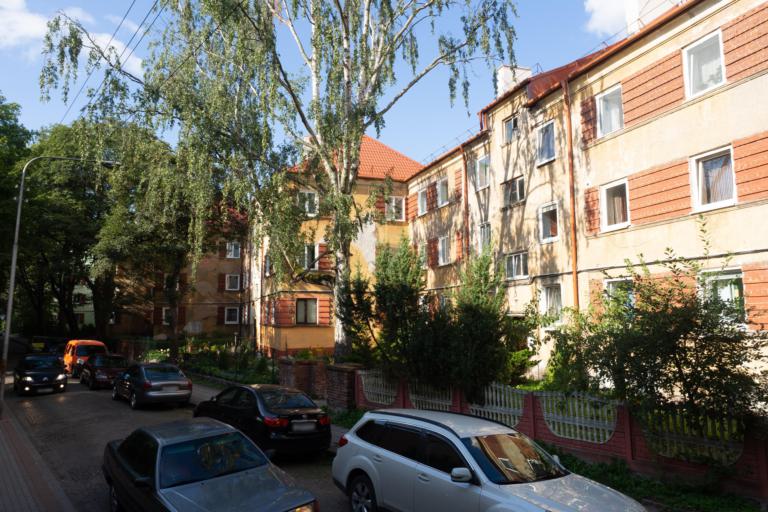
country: RU
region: Kaliningrad
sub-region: Gorod Kaliningrad
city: Kaliningrad
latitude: 54.7267
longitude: 20.4680
